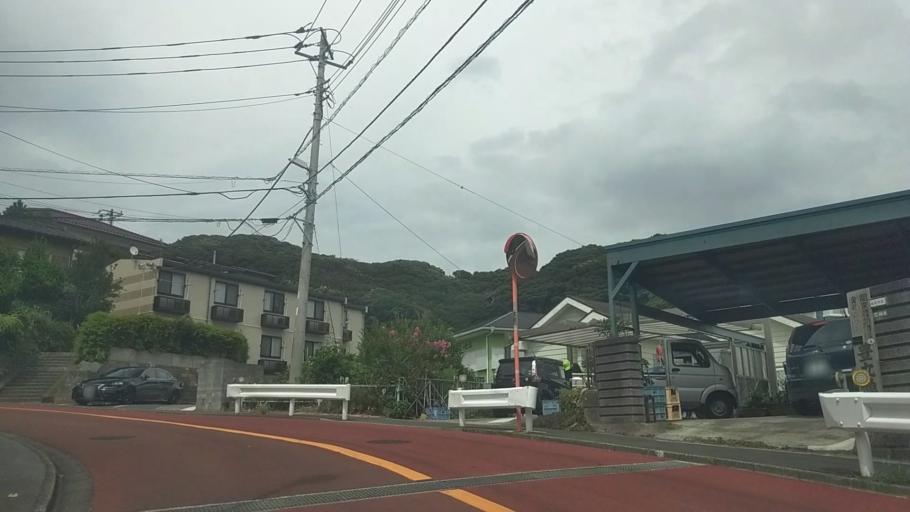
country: JP
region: Kanagawa
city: Yokosuka
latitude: 35.2422
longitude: 139.7257
